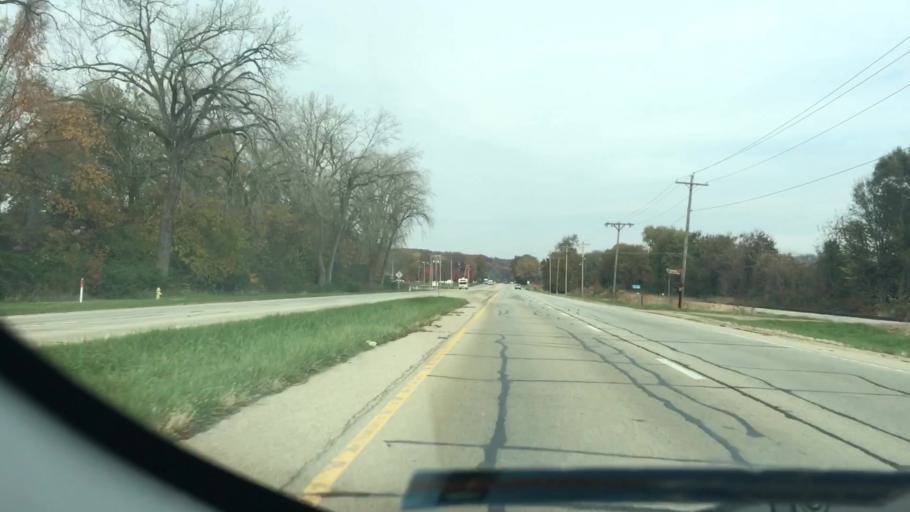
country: US
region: Illinois
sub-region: Peoria County
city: Peoria Heights
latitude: 40.7628
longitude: -89.5676
